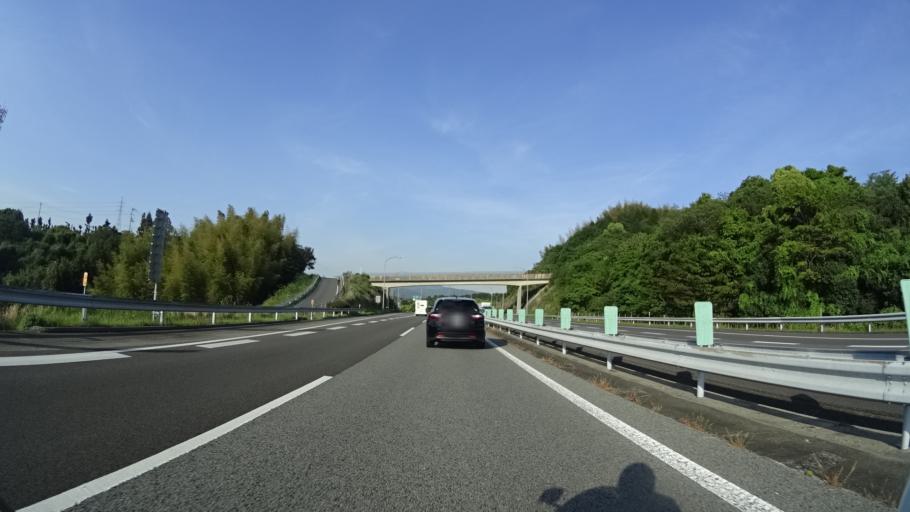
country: JP
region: Ehime
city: Kawanoecho
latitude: 33.9781
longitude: 133.5732
